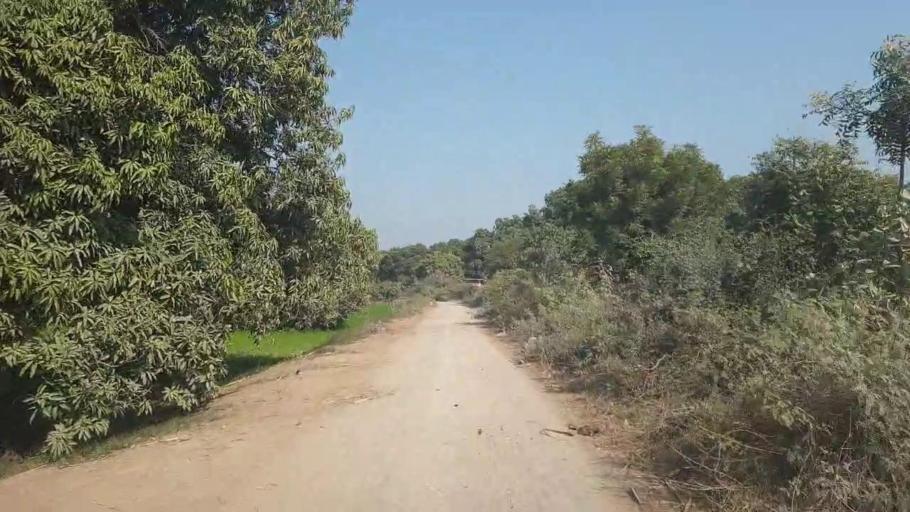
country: PK
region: Sindh
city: Tando Allahyar
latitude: 25.4733
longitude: 68.7840
